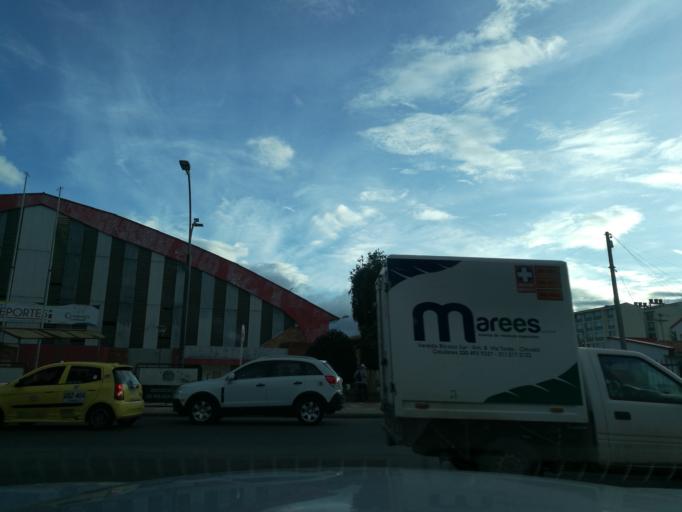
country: CO
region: Boyaca
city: Tunja
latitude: 5.5444
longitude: -73.3543
